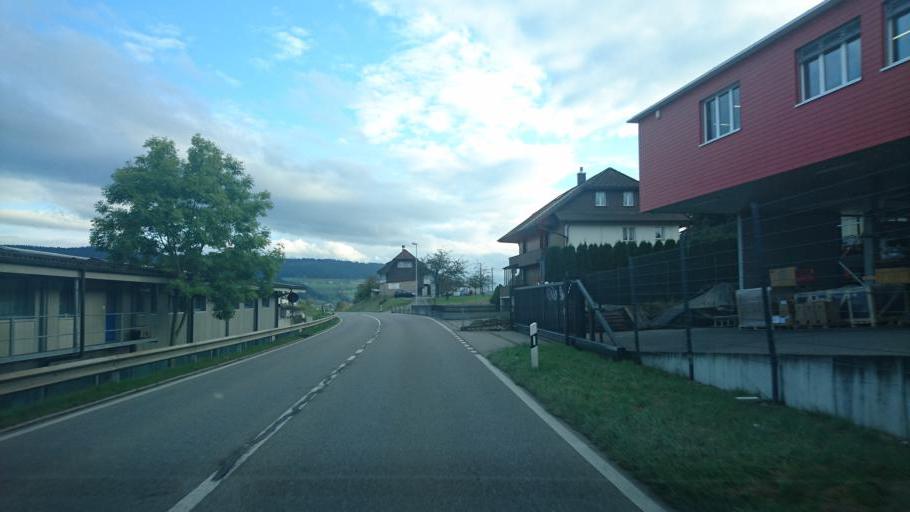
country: CH
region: Bern
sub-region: Bern-Mittelland District
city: Konolfingen
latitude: 46.8991
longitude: 7.6334
